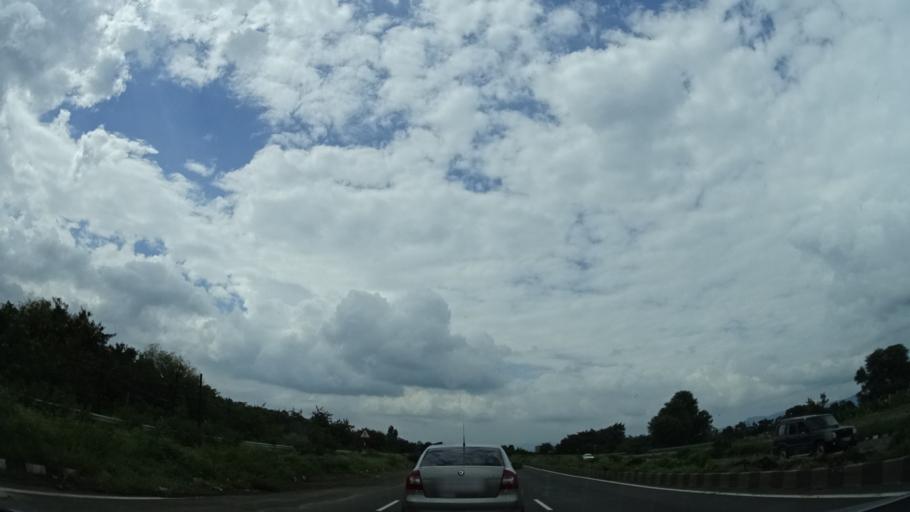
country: IN
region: Maharashtra
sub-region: Satara Division
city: Satara
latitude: 17.8007
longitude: 73.9759
